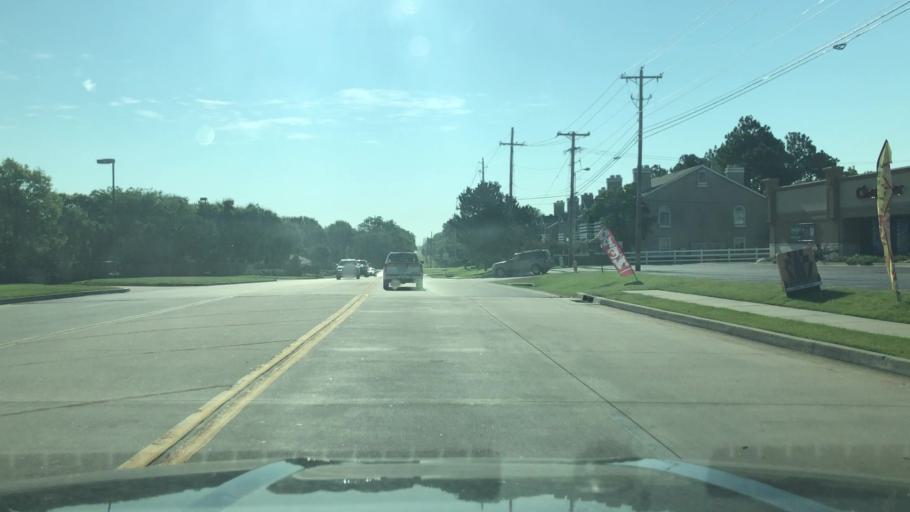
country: US
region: Oklahoma
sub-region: Tulsa County
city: Jenks
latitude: 36.0318
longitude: -95.9030
